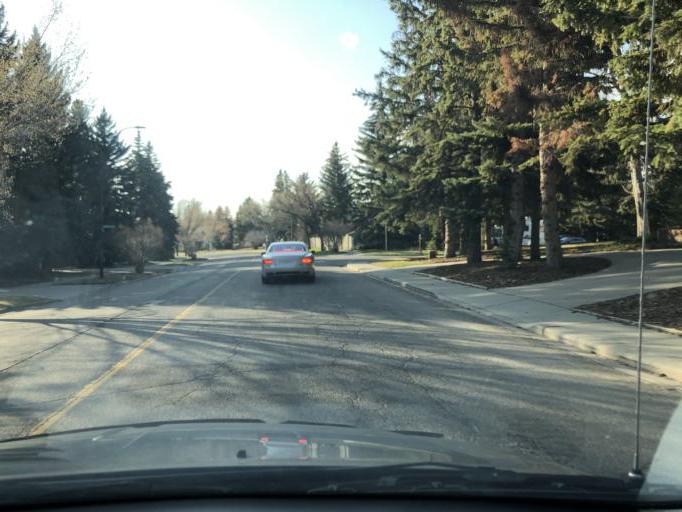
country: CA
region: Alberta
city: Calgary
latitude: 50.9660
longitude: -114.1033
